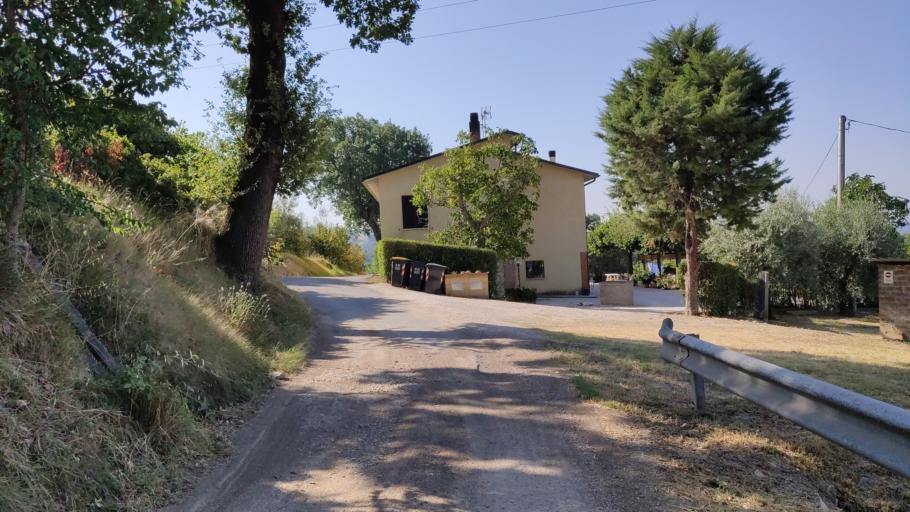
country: IT
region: Umbria
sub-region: Provincia di Terni
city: Amelia
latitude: 42.5292
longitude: 12.4105
